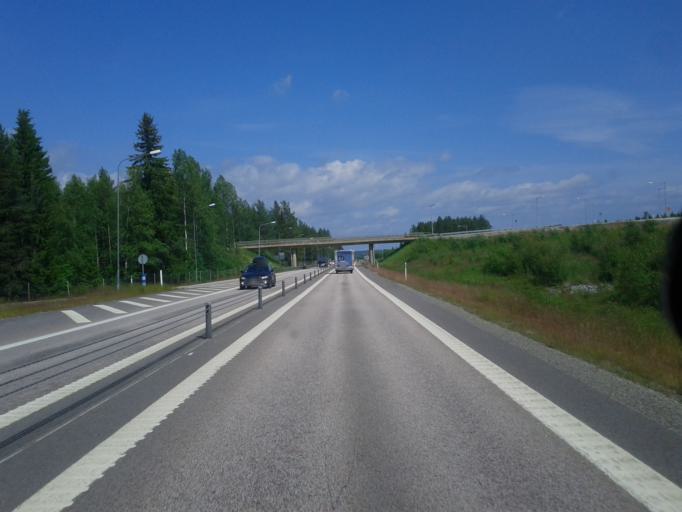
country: SE
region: Vaesterbotten
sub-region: Nordmalings Kommun
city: Nordmaling
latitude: 63.5479
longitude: 19.4127
